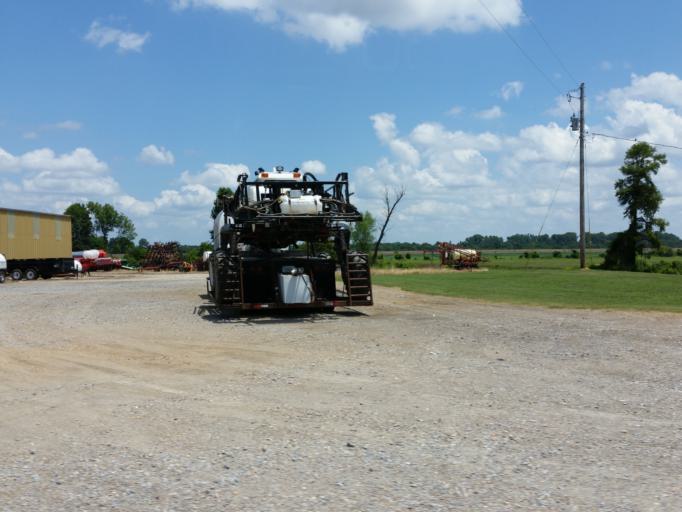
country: US
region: Kentucky
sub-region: Fulton County
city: Hickman
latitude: 36.5507
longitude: -89.2708
